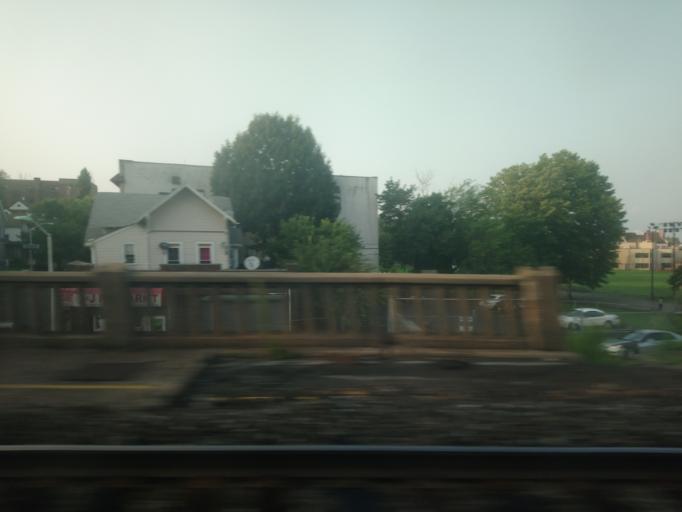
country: US
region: New Jersey
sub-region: Essex County
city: East Orange
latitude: 40.7588
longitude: -74.2035
